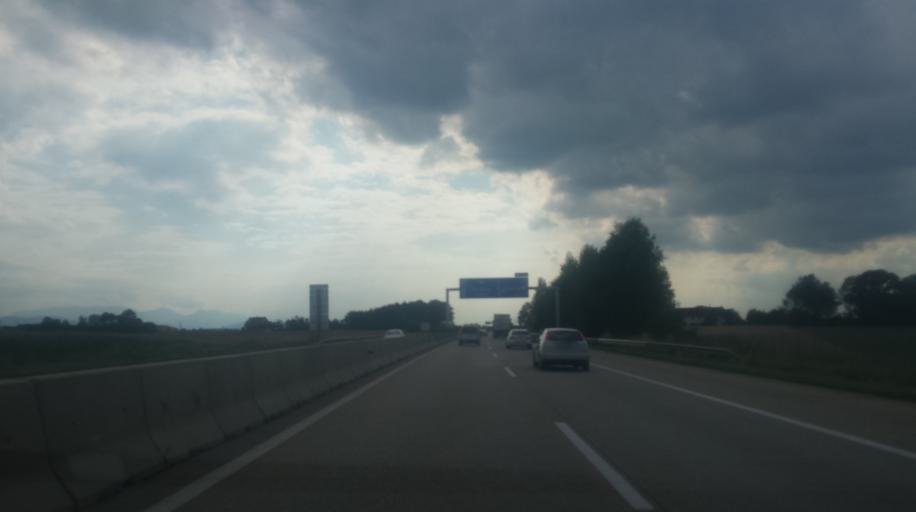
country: AT
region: Upper Austria
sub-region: Wels-Land
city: Sattledt
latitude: 48.0479
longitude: 14.0097
